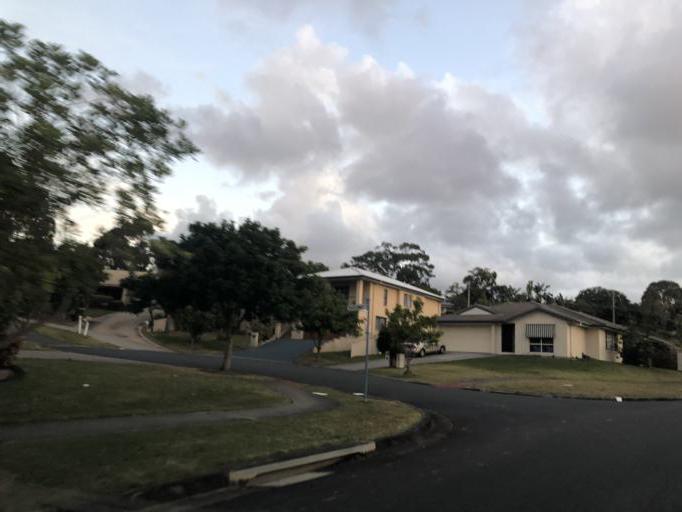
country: AU
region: New South Wales
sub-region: Coffs Harbour
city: Woolgoolga
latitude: -30.0955
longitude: 153.1923
